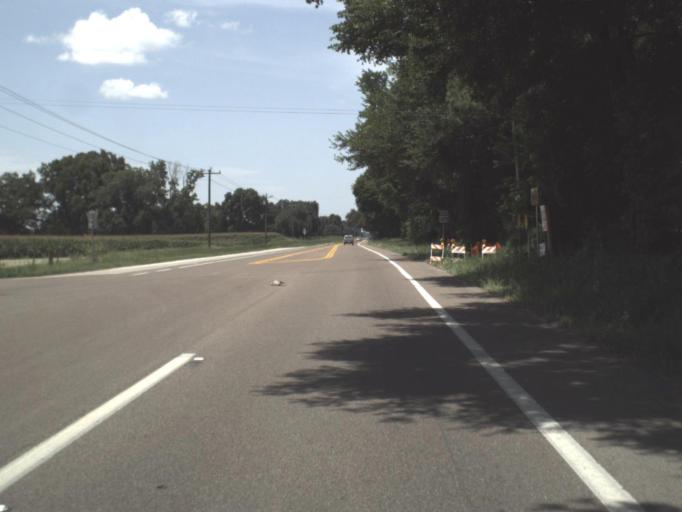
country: US
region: Florida
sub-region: Gilchrist County
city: Trenton
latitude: 29.6936
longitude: -82.8573
